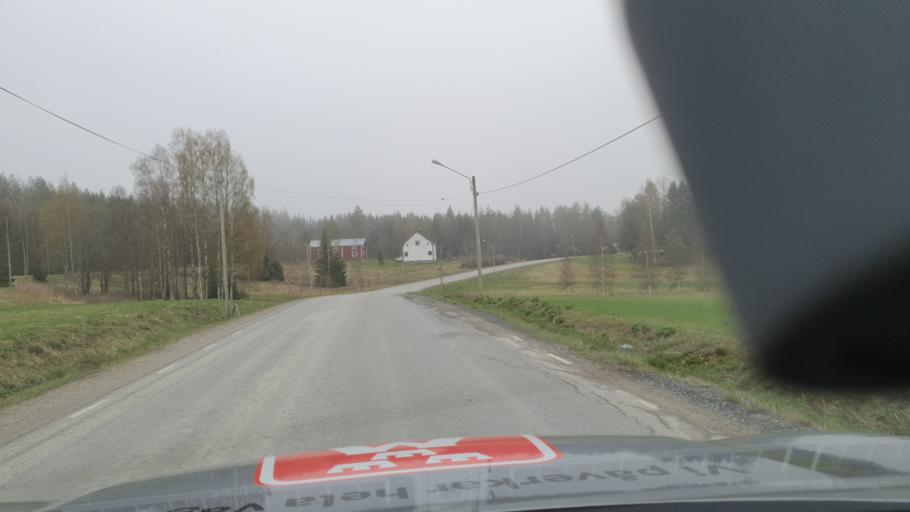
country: SE
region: Vaesternorrland
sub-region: OErnskoeldsviks Kommun
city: Husum
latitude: 63.5808
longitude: 19.0264
